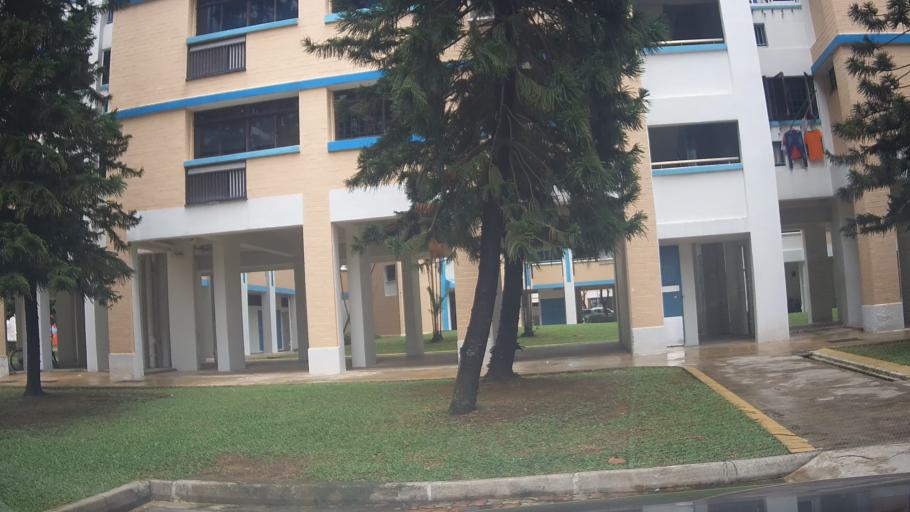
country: MY
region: Johor
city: Johor Bahru
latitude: 1.4478
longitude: 103.8000
